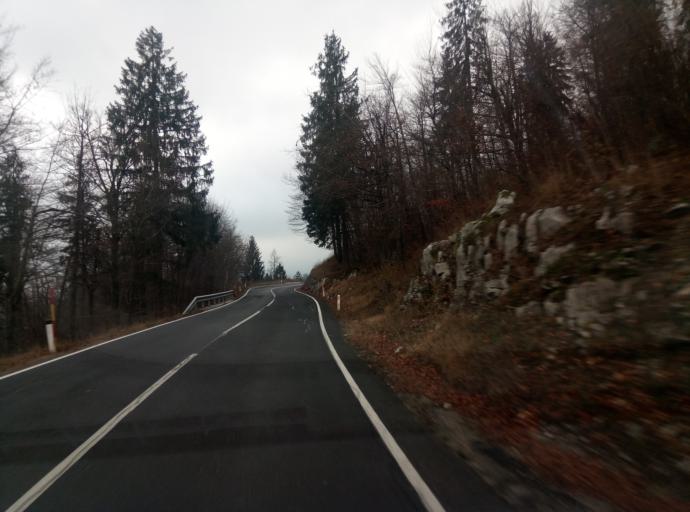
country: SI
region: Idrija
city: Idrija
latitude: 45.9464
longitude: 14.0780
